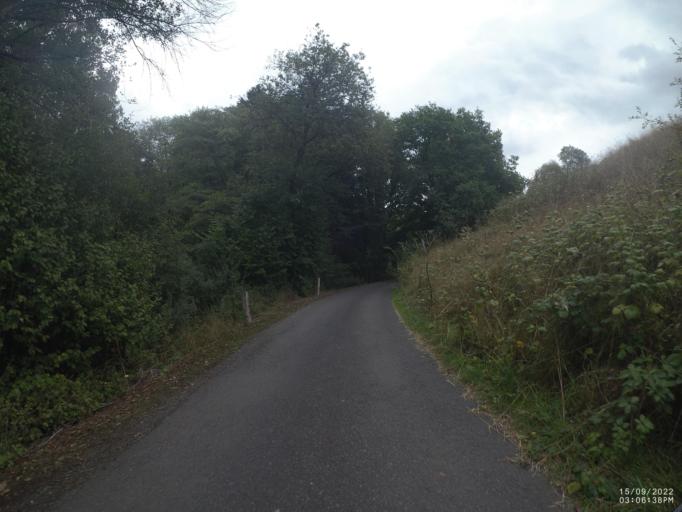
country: DE
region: Rheinland-Pfalz
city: Bongard
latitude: 50.2935
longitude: 6.8151
